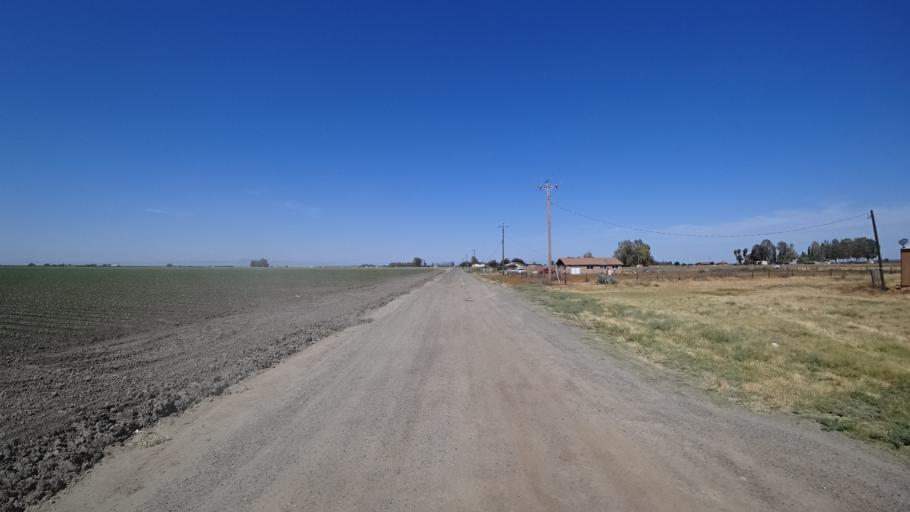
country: US
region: California
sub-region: Kings County
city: Stratford
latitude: 36.1967
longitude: -119.7764
